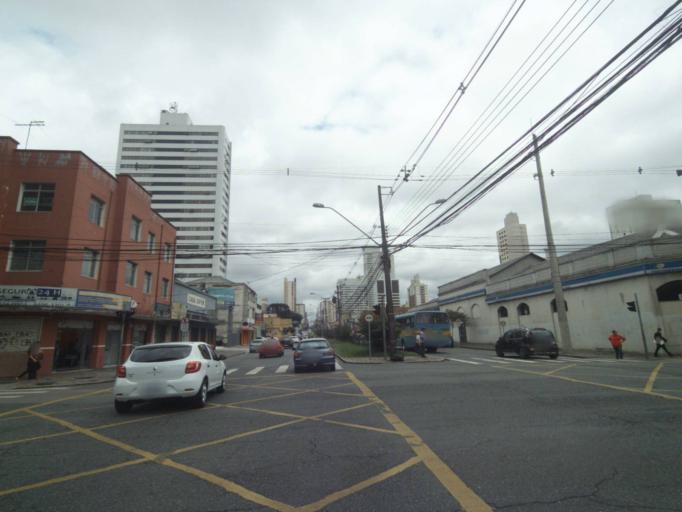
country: BR
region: Parana
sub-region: Curitiba
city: Curitiba
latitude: -25.4351
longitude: -49.2642
